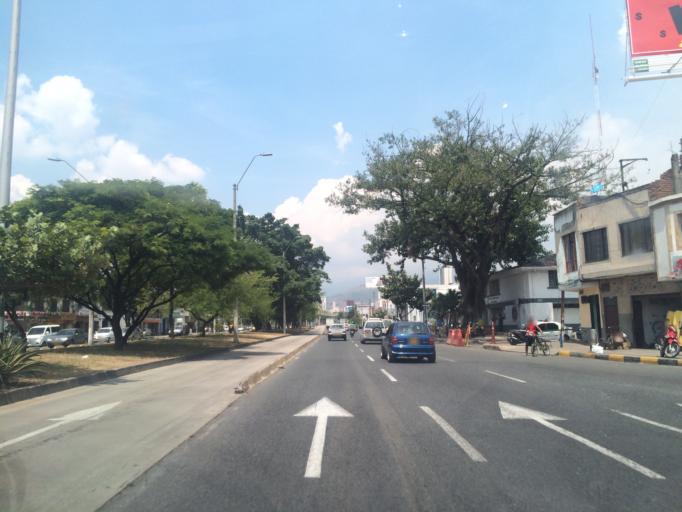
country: CO
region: Valle del Cauca
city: Cali
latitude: 3.4645
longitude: -76.5153
